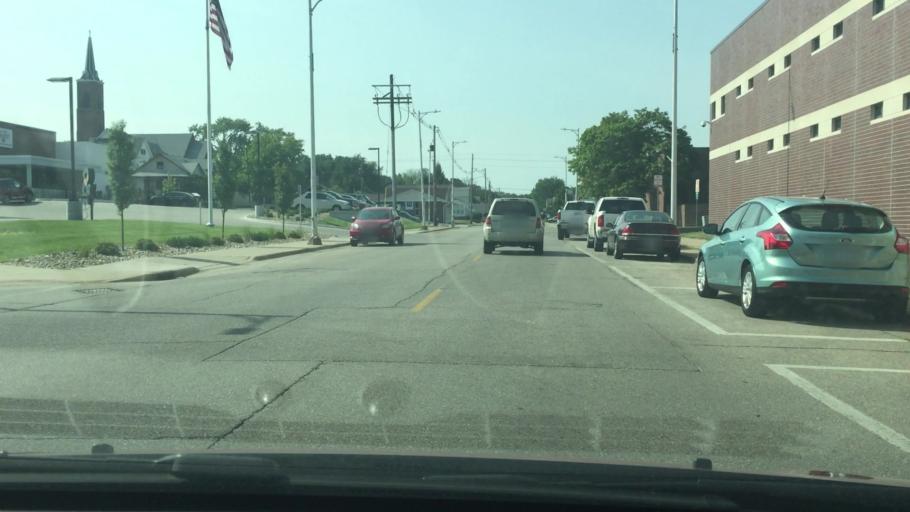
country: US
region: Iowa
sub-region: Muscatine County
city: Muscatine
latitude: 41.4241
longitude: -91.0451
